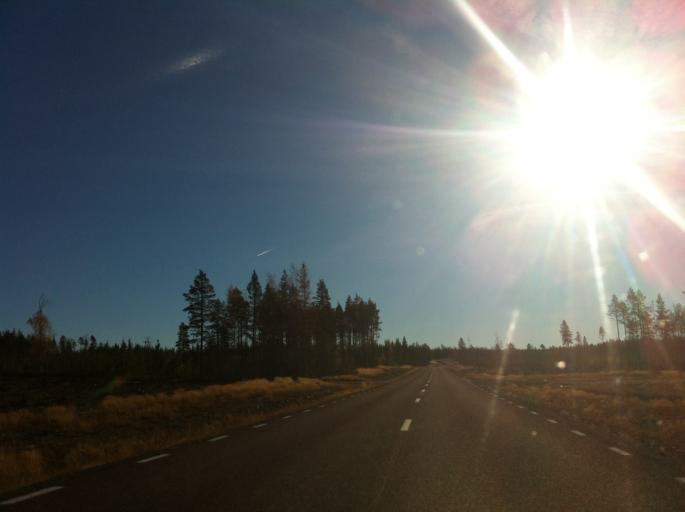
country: SE
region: Dalarna
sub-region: Alvdalens Kommun
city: AElvdalen
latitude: 61.6290
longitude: 13.2314
